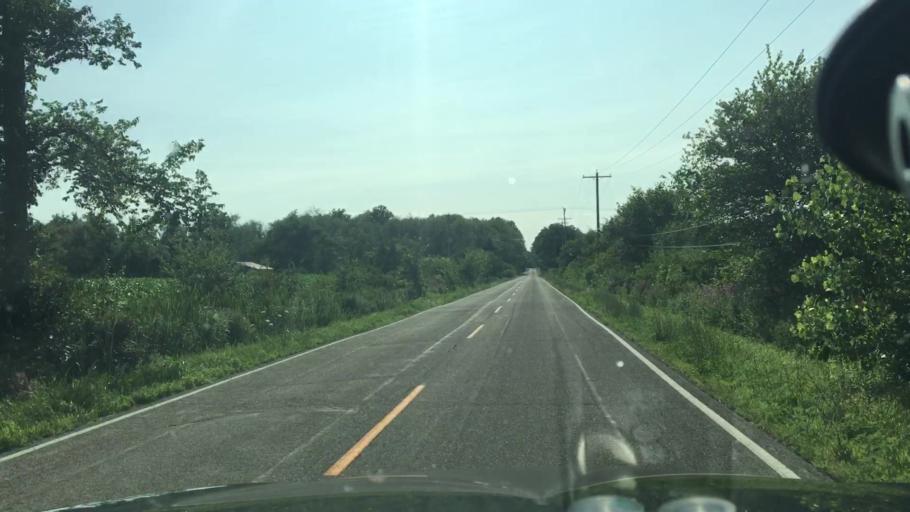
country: US
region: New York
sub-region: Erie County
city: North Collins
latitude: 42.6197
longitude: -78.9370
